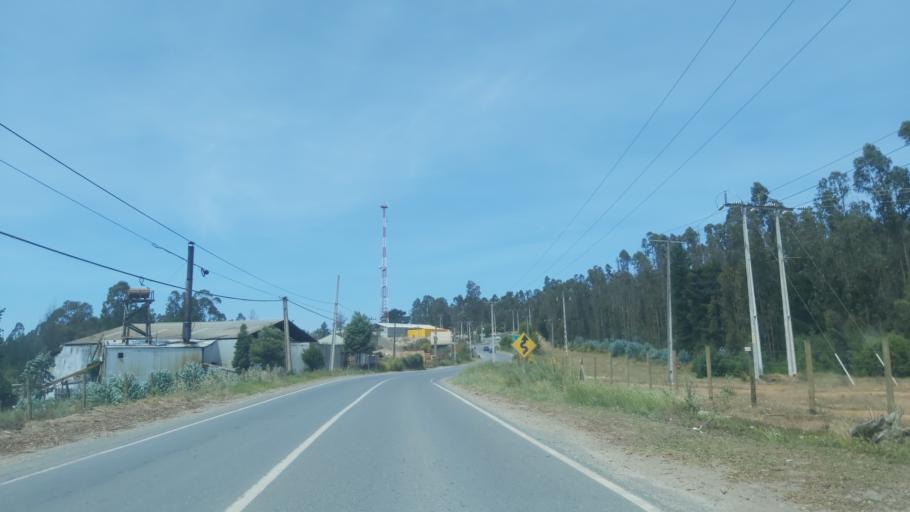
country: CL
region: Maule
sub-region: Provincia de Talca
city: Constitucion
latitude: -35.3674
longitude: -72.4073
